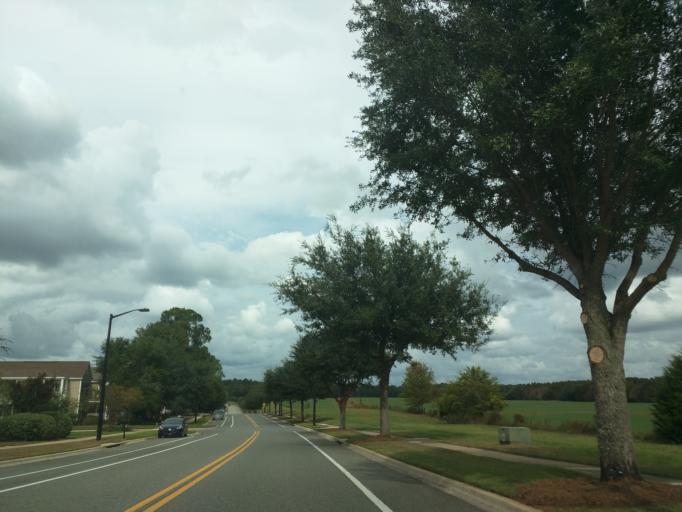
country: US
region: Florida
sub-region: Leon County
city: Tallahassee
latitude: 30.3977
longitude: -84.2094
